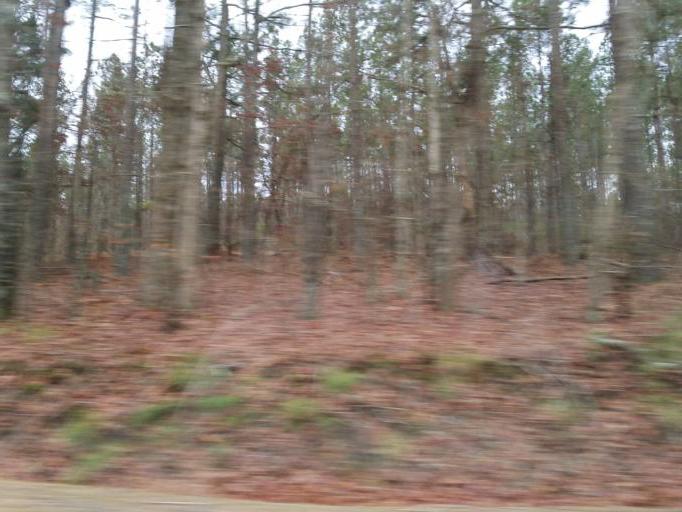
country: US
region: Georgia
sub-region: Dawson County
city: Dawsonville
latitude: 34.4476
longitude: -84.1167
